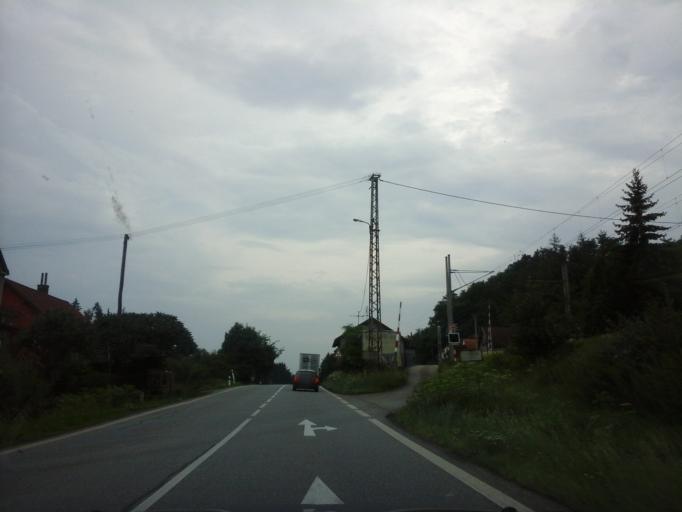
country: CZ
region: South Moravian
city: Svitavka
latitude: 49.5152
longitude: 16.5853
